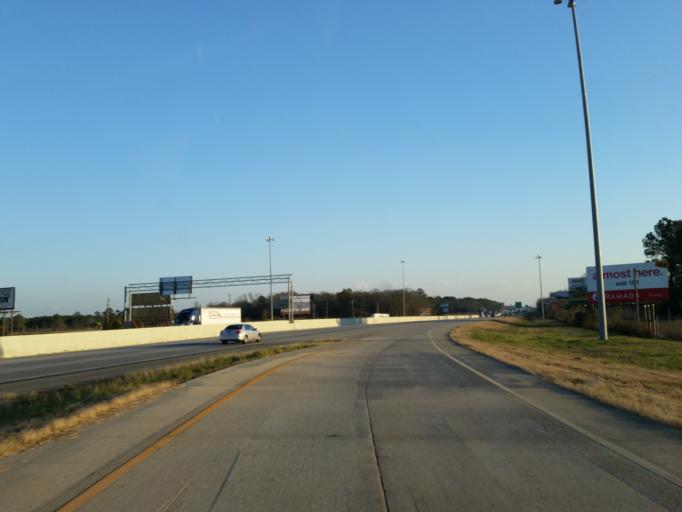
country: US
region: Georgia
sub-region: Crisp County
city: Cordele
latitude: 32.0004
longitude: -83.7584
